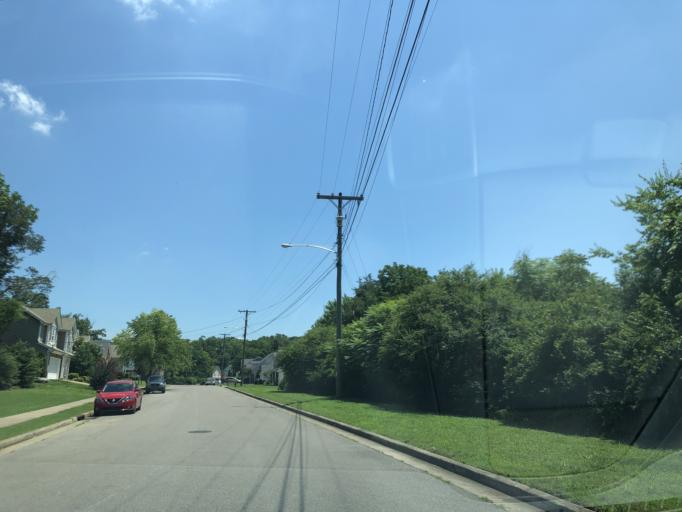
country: US
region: Tennessee
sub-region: Williamson County
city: Nolensville
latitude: 36.0105
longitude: -86.6521
